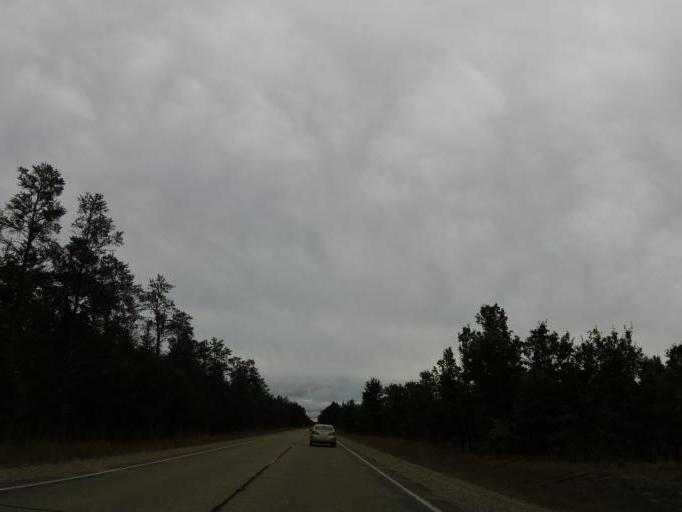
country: US
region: Michigan
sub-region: Roscommon County
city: Roscommon
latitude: 44.4757
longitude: -84.5540
